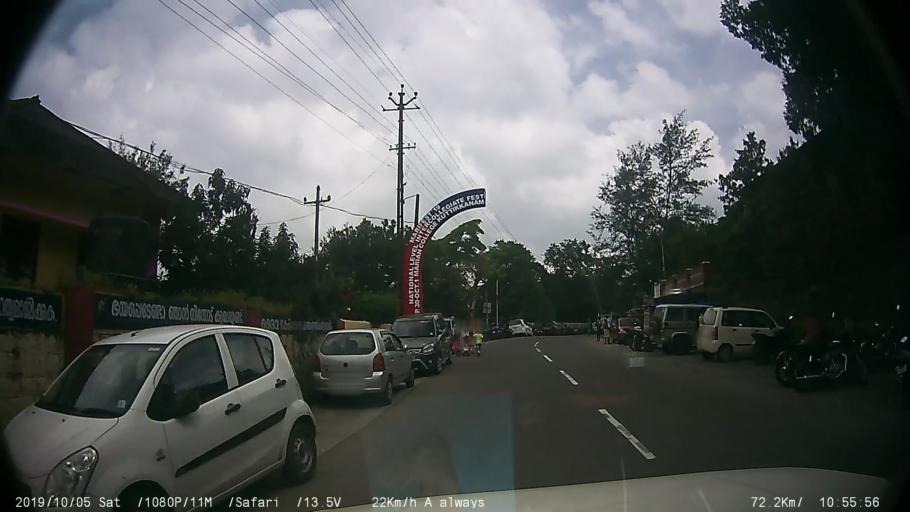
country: IN
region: Kerala
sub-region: Kottayam
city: Erattupetta
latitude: 9.5832
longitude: 76.9711
